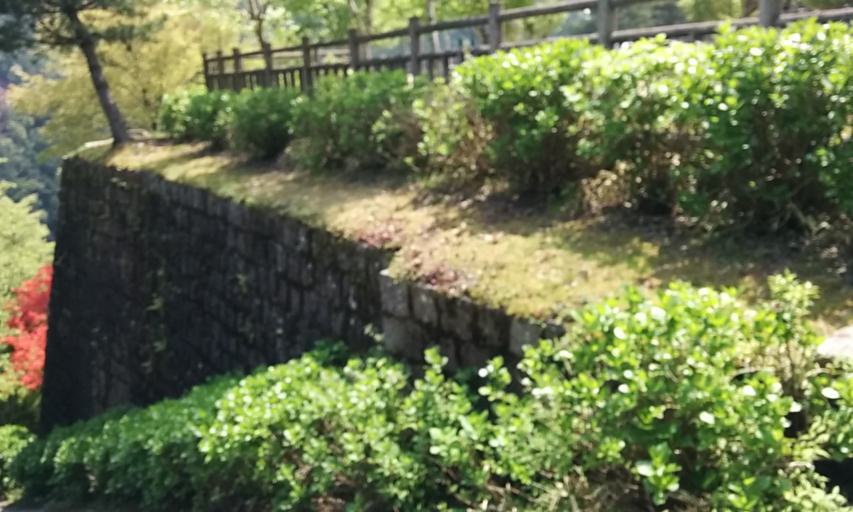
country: JP
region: Ehime
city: Niihama
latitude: 33.8775
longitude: 133.3135
